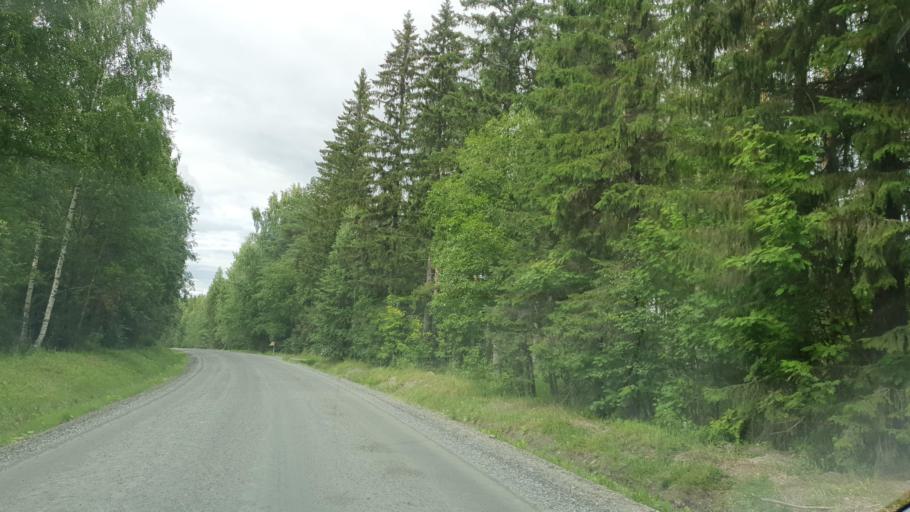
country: FI
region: Northern Savo
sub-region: Ylae-Savo
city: Iisalmi
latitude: 63.5309
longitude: 27.0887
